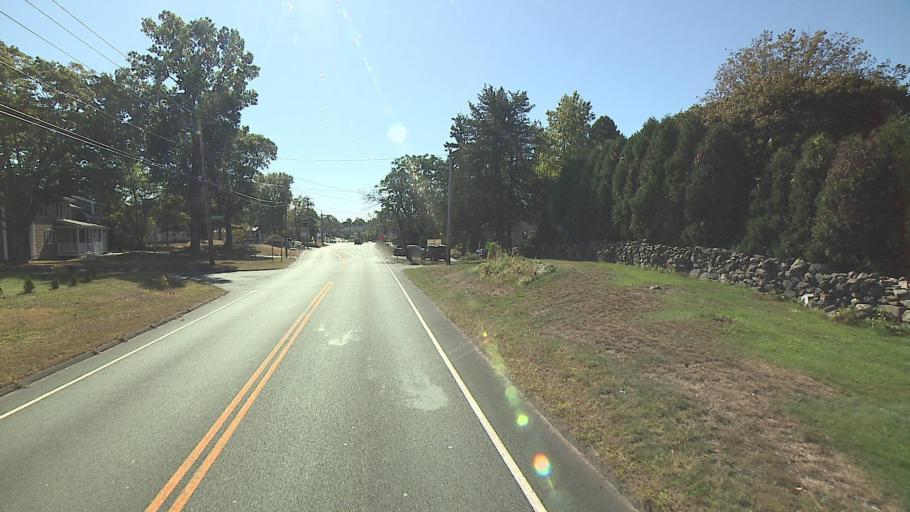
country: US
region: Connecticut
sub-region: New Haven County
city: Orange
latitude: 41.2696
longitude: -73.0012
